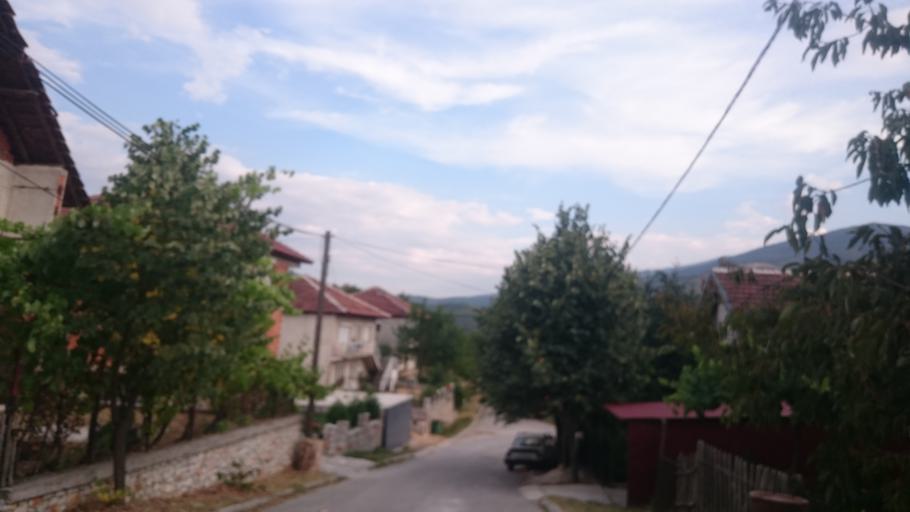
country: MK
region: Makedonski Brod
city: Makedonski Brod
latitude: 41.5197
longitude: 21.2157
